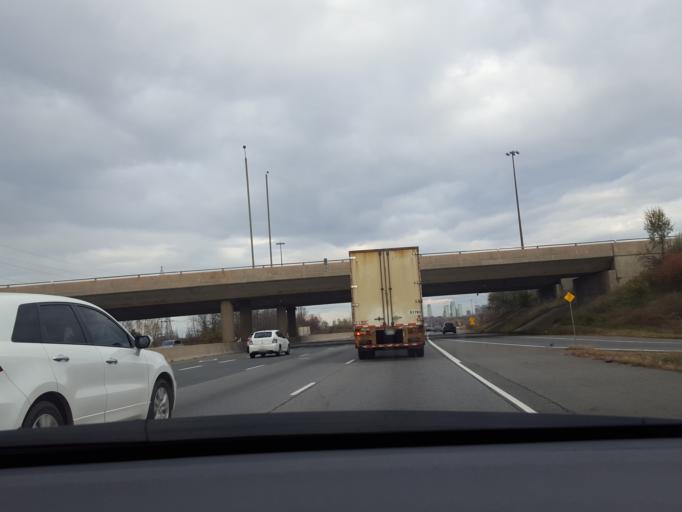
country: CA
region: Ontario
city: Mississauga
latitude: 43.5533
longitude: -79.6973
